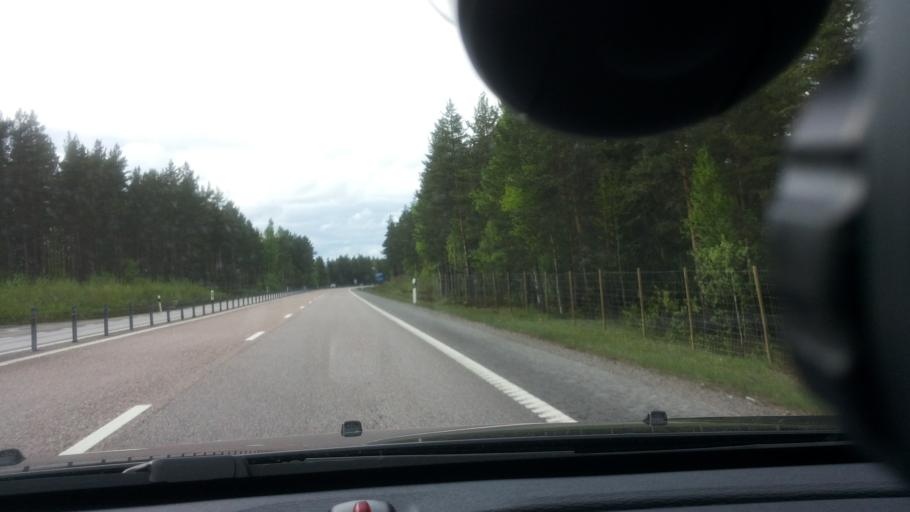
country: SE
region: Gaevleborg
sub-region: Gavle Kommun
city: Norrsundet
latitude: 60.9933
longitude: 17.0004
